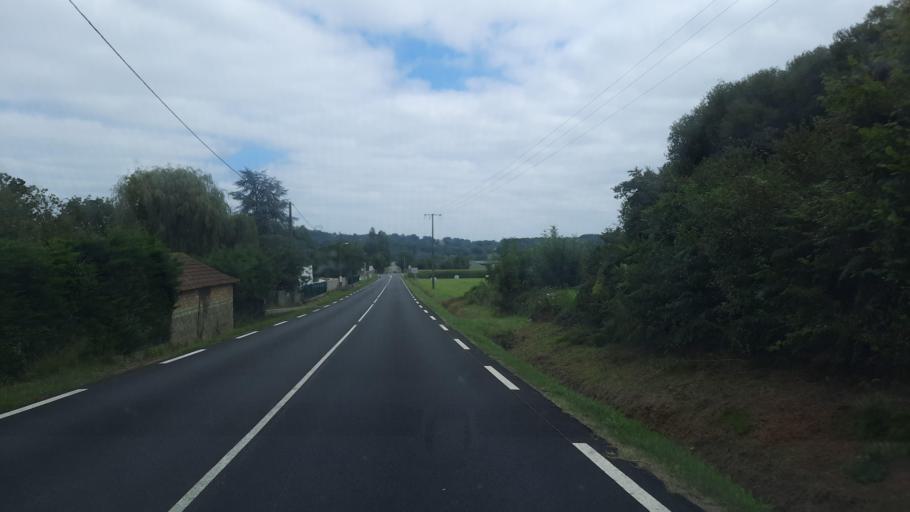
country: FR
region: Midi-Pyrenees
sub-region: Departement des Hautes-Pyrenees
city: Orleix
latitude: 43.2739
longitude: 0.1700
